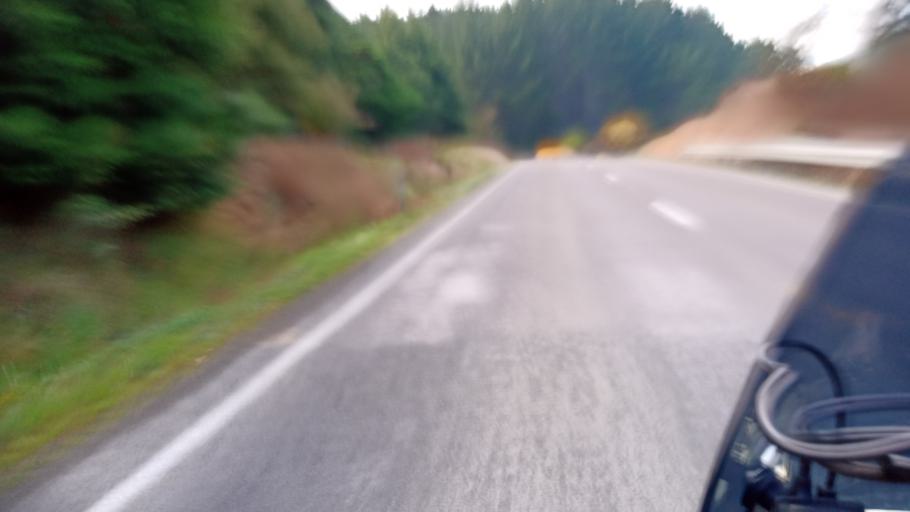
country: NZ
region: Gisborne
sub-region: Gisborne District
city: Gisborne
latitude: -38.8371
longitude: 177.8957
